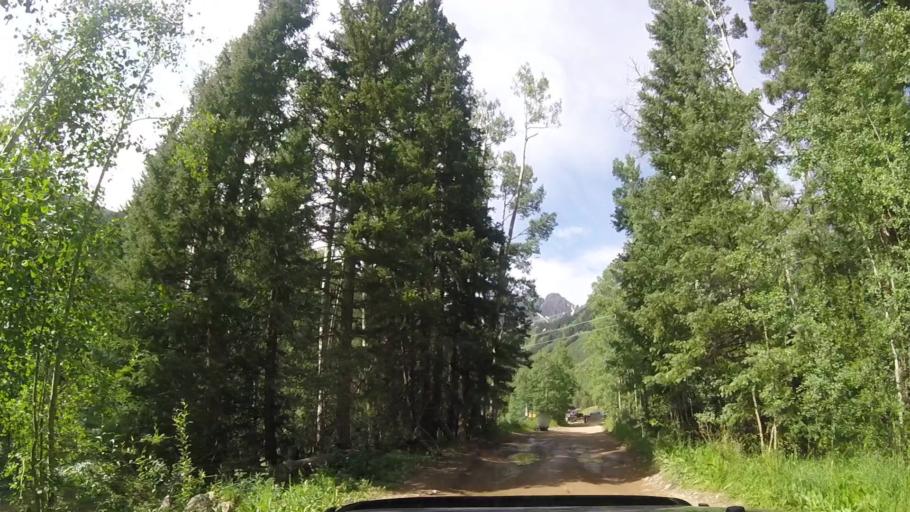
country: US
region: Colorado
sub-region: San Miguel County
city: Telluride
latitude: 37.8573
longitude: -107.8231
